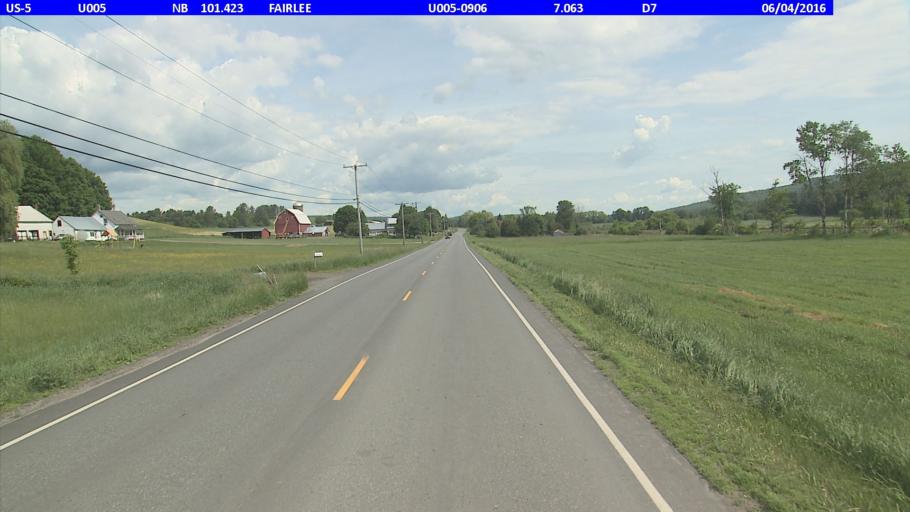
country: US
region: New Hampshire
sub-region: Grafton County
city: Orford
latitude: 43.9583
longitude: -72.1154
